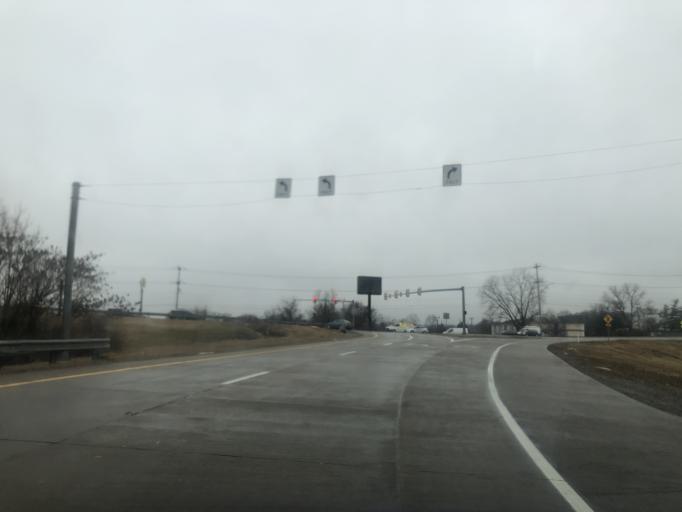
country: US
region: Tennessee
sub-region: Davidson County
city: Oak Hill
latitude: 36.0855
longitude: -86.6987
